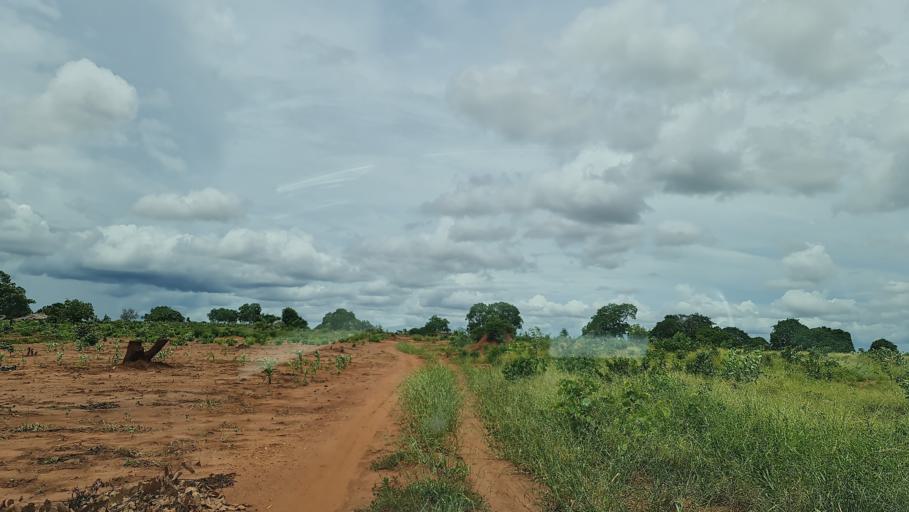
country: MZ
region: Nampula
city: Nacala
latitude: -14.7865
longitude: 39.9785
